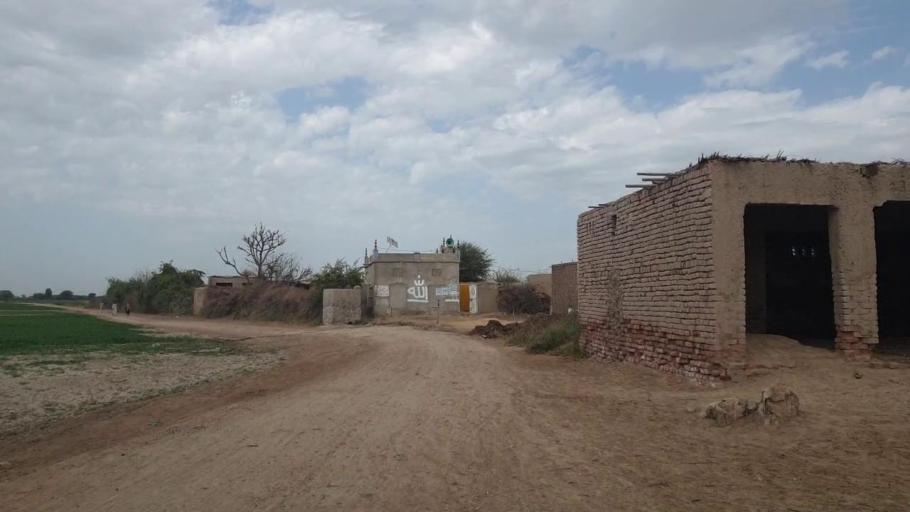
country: PK
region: Sindh
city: Hala
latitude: 25.9389
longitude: 68.4077
